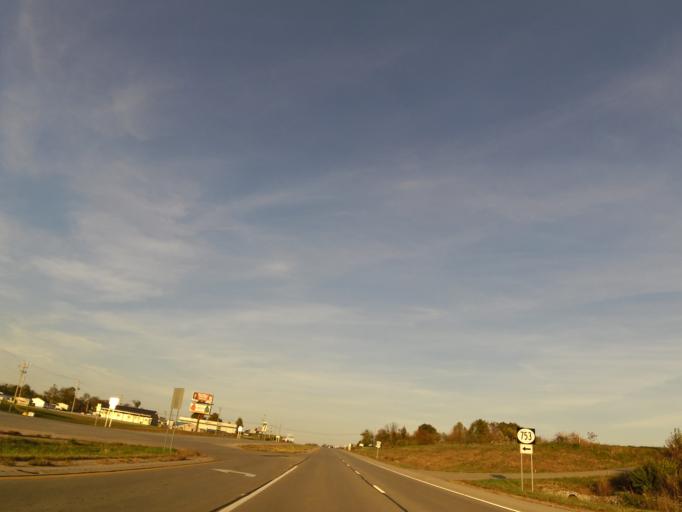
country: US
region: Kentucky
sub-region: Garrard County
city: Lancaster
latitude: 37.7059
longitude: -84.6571
